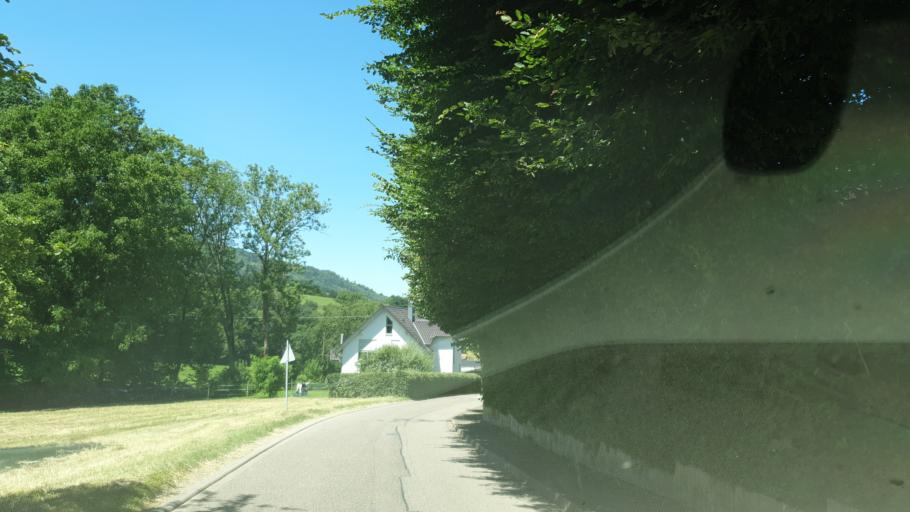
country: DE
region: Baden-Wuerttemberg
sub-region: Freiburg Region
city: Au
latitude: 47.9489
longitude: 7.8303
